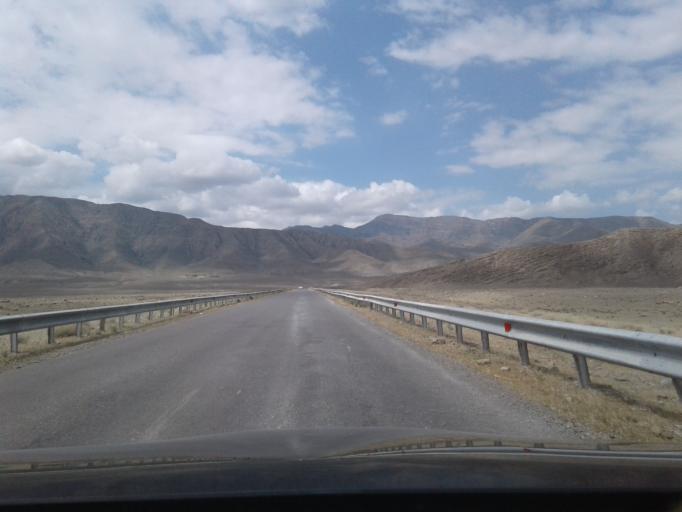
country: TM
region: Ahal
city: Baharly
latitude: 38.5090
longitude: 57.1285
